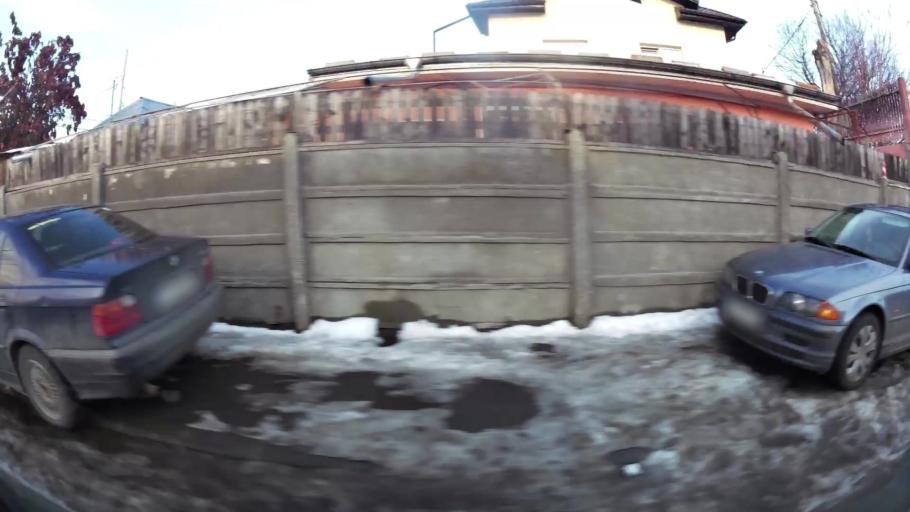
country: RO
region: Bucuresti
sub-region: Municipiul Bucuresti
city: Bucuresti
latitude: 44.3873
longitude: 26.0805
